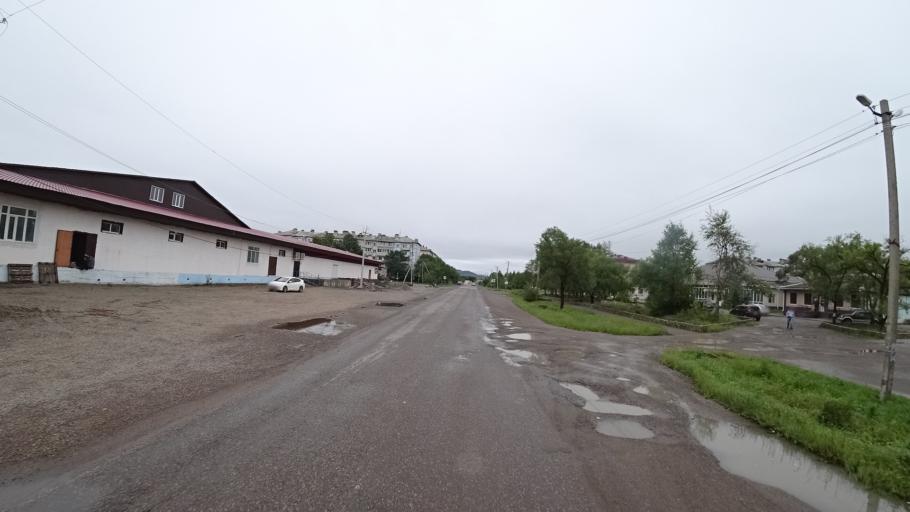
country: RU
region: Primorskiy
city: Monastyrishche
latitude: 44.2050
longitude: 132.4443
